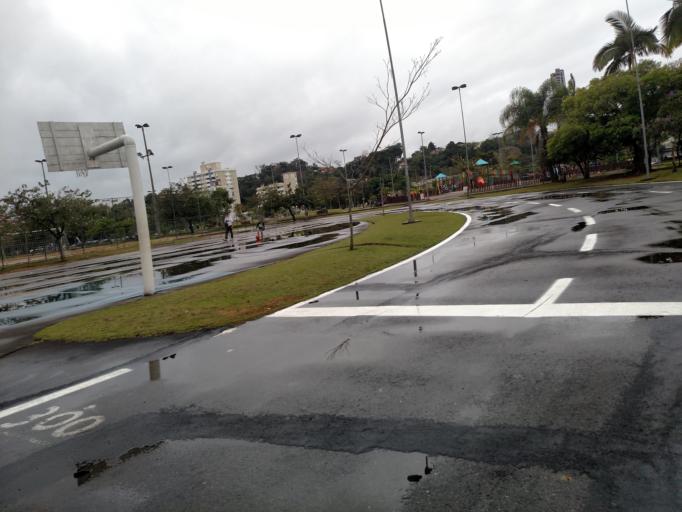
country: BR
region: Santa Catarina
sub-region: Blumenau
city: Blumenau
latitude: -26.9141
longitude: -49.0871
